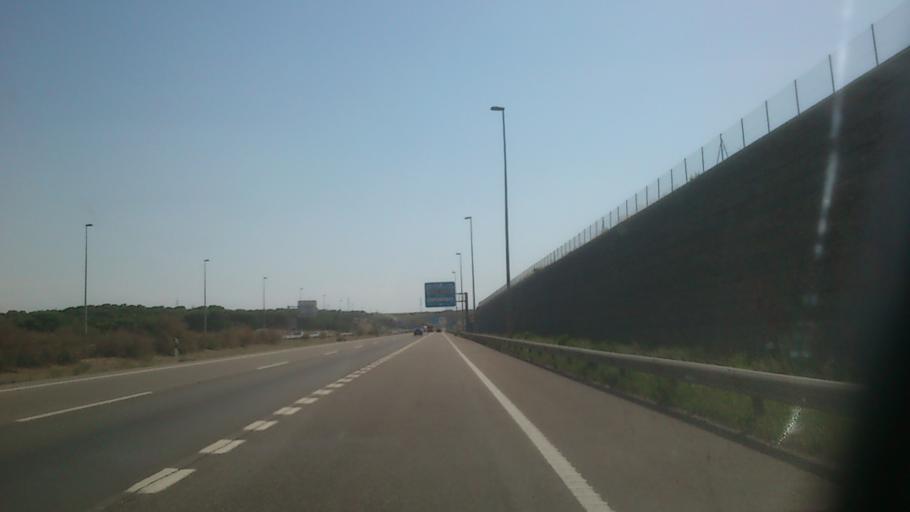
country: ES
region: Aragon
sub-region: Provincia de Zaragoza
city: Zaragoza
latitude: 41.6159
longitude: -0.8696
